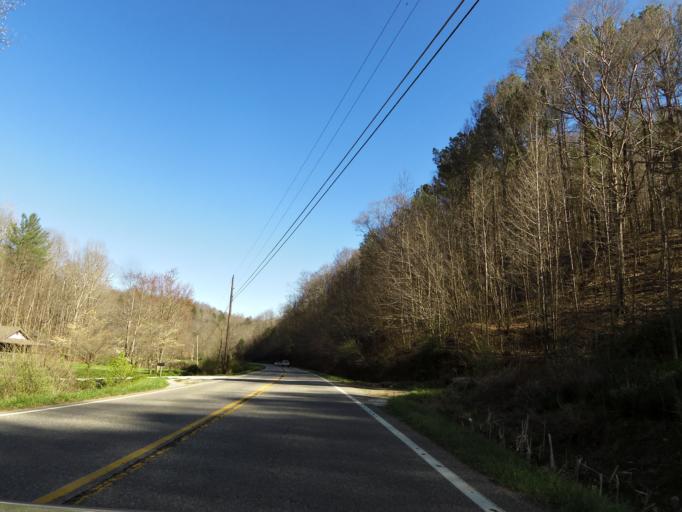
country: US
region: Tennessee
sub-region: Scott County
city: Oneida
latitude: 36.4751
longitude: -84.4856
